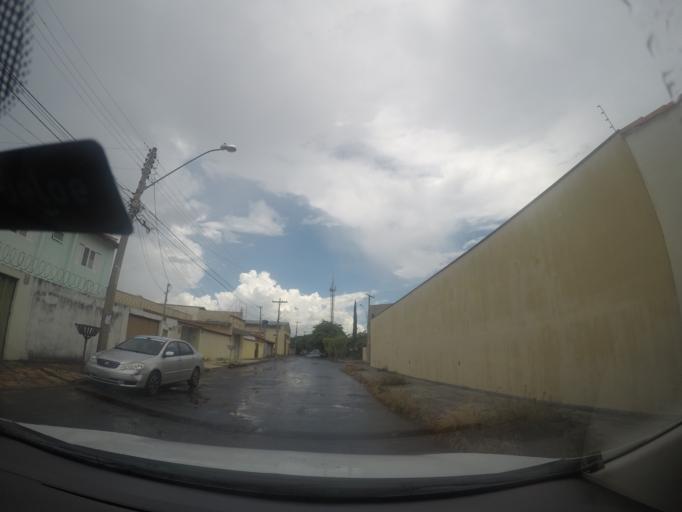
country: BR
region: Goias
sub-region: Goiania
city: Goiania
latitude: -16.6802
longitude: -49.2876
